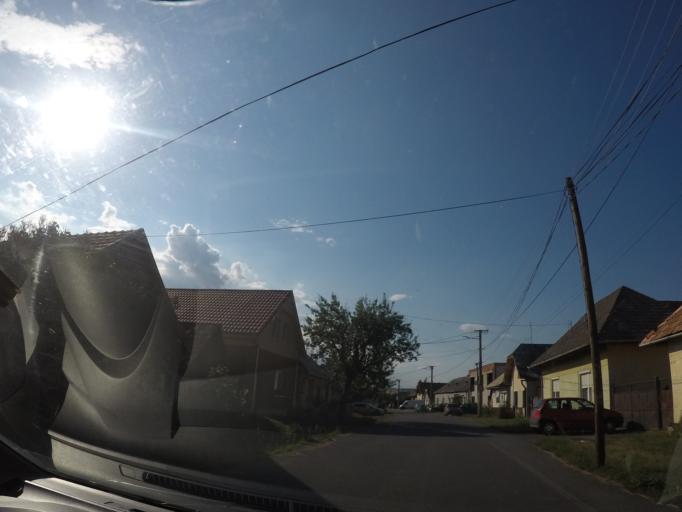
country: SK
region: Banskobystricky
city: Dudince
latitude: 48.1852
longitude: 18.8453
